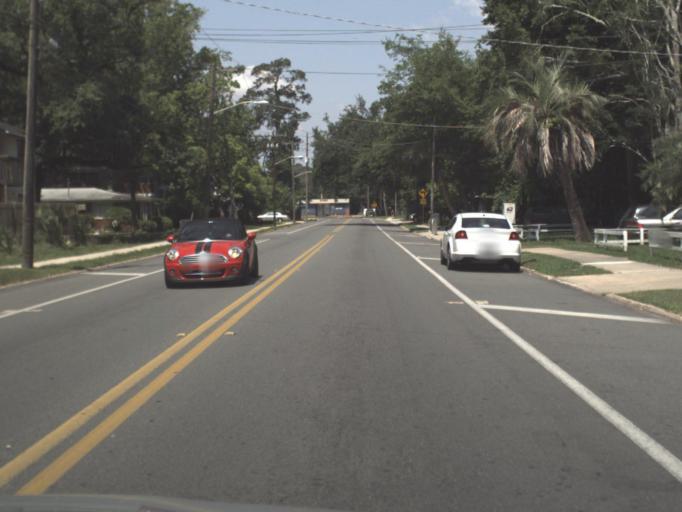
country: US
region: Florida
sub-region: Duval County
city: Jacksonville
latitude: 30.3132
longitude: -81.7152
